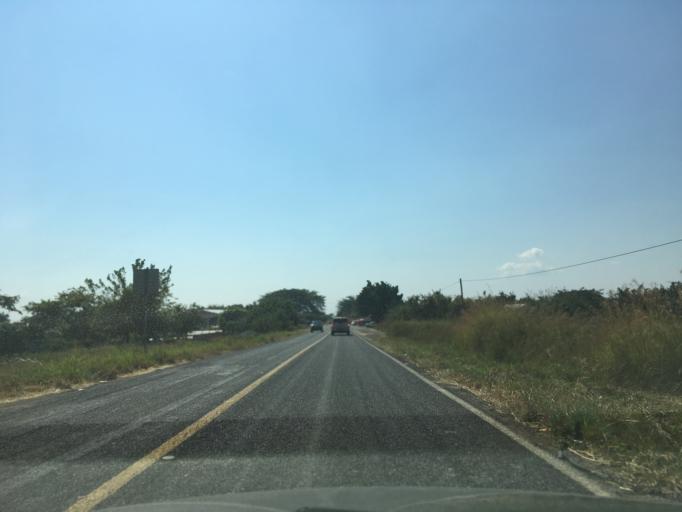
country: MX
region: Michoacan
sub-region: Gabriel Zamora
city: Lombardia
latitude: 19.2192
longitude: -102.0457
